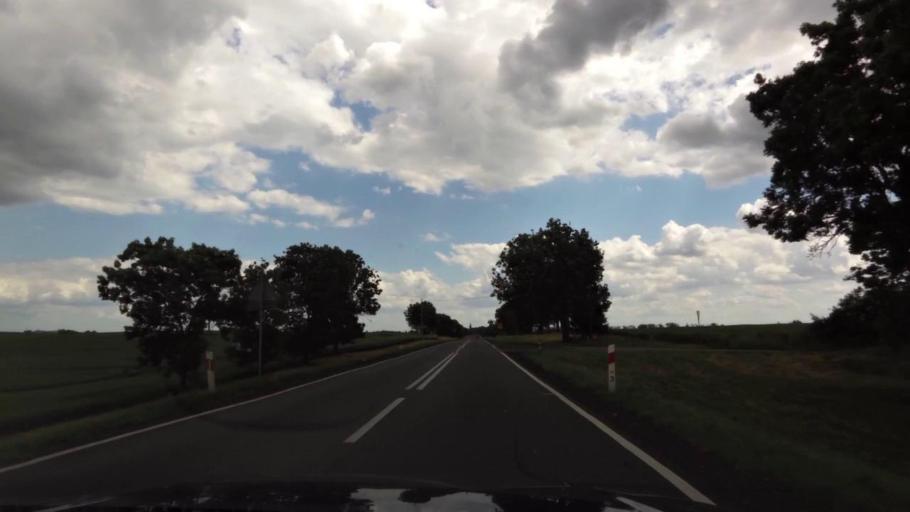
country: PL
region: West Pomeranian Voivodeship
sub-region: Powiat mysliborski
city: Mysliborz
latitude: 52.9586
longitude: 14.7646
